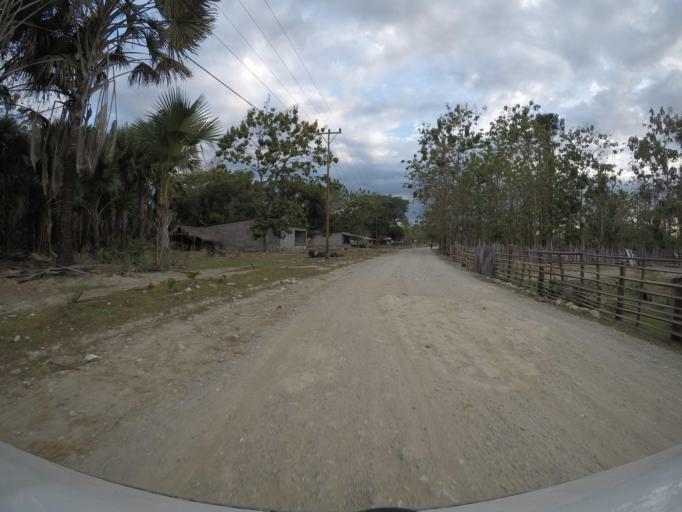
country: TL
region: Bobonaro
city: Maliana
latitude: -8.8783
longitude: 125.2124
